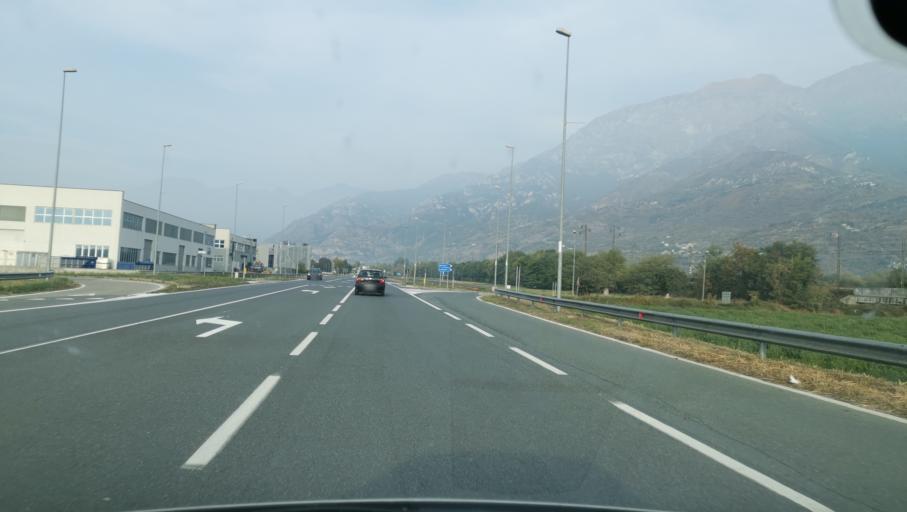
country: IT
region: Piedmont
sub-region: Provincia di Torino
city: Bruzolo
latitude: 45.1321
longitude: 7.1940
